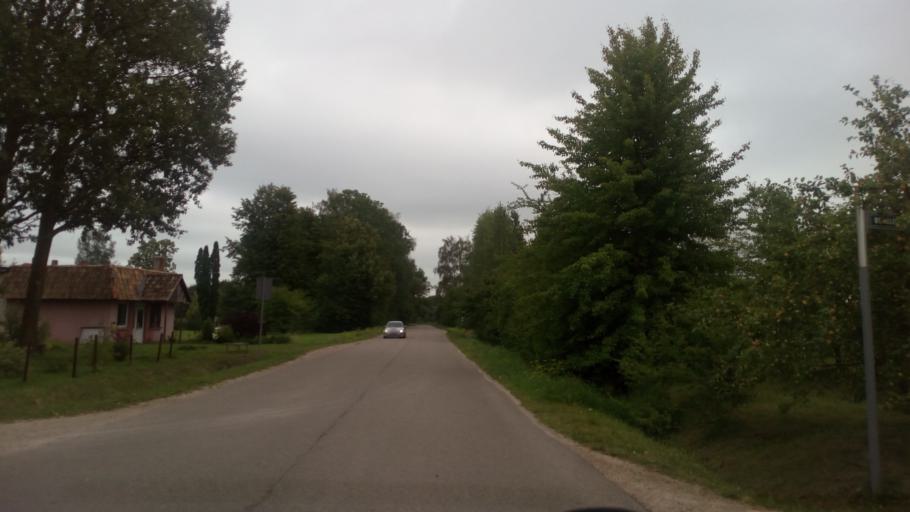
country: LV
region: Rundales
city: Pilsrundale
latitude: 56.4277
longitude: 23.9833
